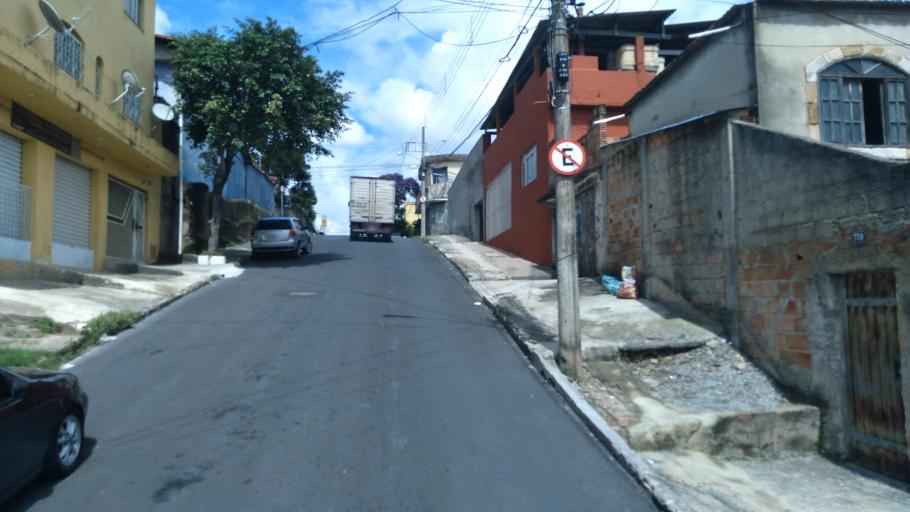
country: BR
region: Minas Gerais
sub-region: Belo Horizonte
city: Belo Horizonte
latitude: -19.8854
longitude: -43.8987
